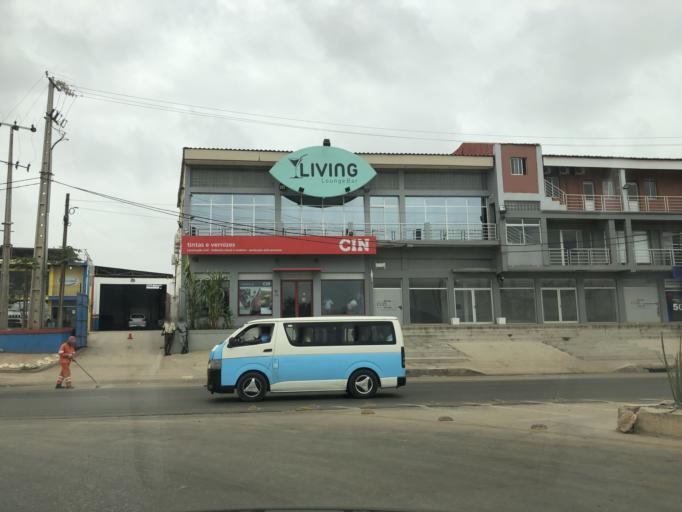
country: AO
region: Luanda
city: Luanda
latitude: -8.8942
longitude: 13.1899
